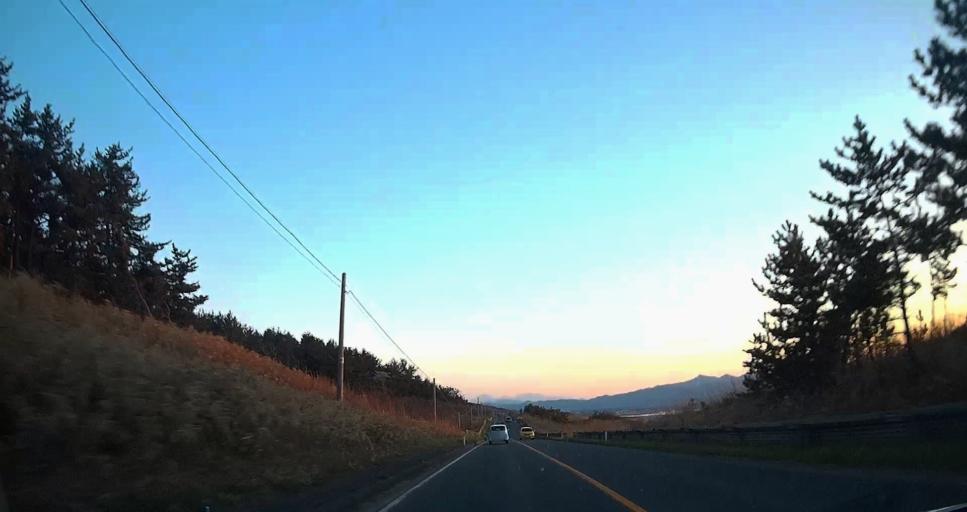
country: JP
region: Aomori
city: Misawa
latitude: 40.8912
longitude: 141.1652
